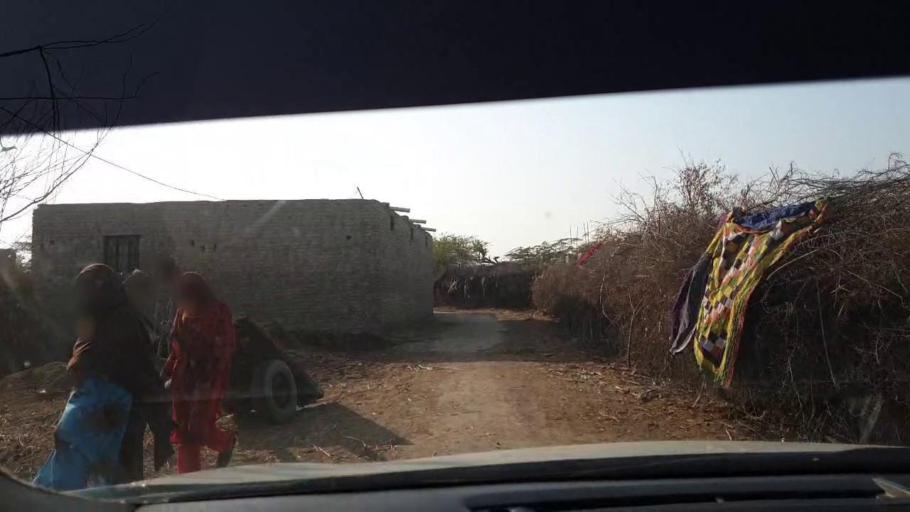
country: PK
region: Sindh
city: Berani
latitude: 25.8452
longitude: 68.7798
